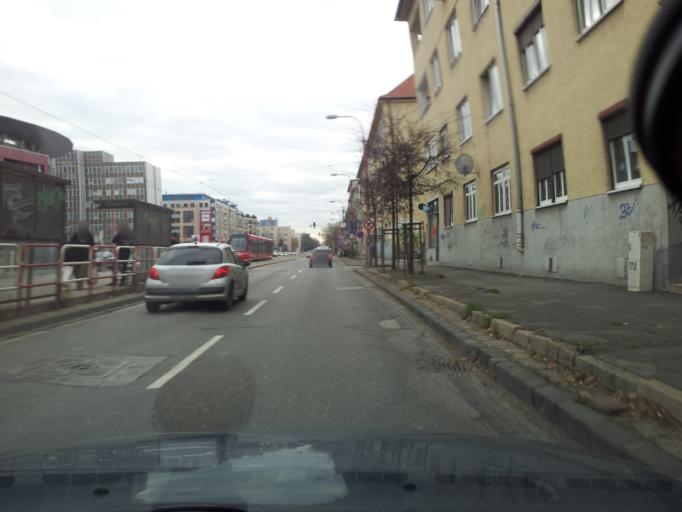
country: SK
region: Bratislavsky
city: Bratislava
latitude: 48.1693
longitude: 17.1387
